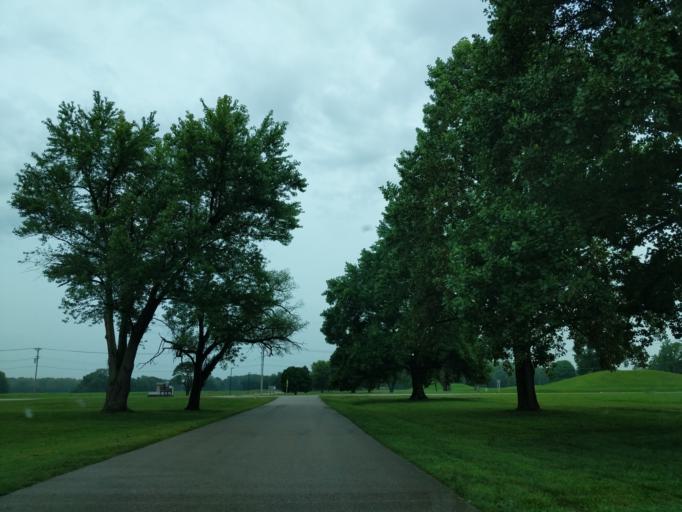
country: US
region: Illinois
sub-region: Saint Clair County
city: Fairmont City
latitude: 38.6596
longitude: -90.0589
